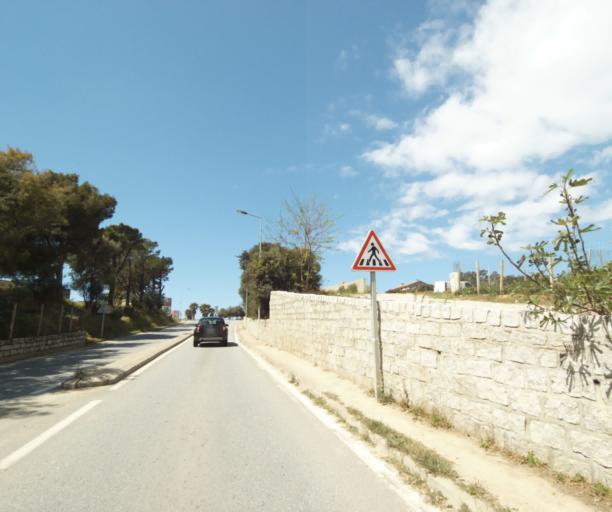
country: FR
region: Corsica
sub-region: Departement de la Corse-du-Sud
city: Propriano
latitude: 41.6690
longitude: 8.9200
